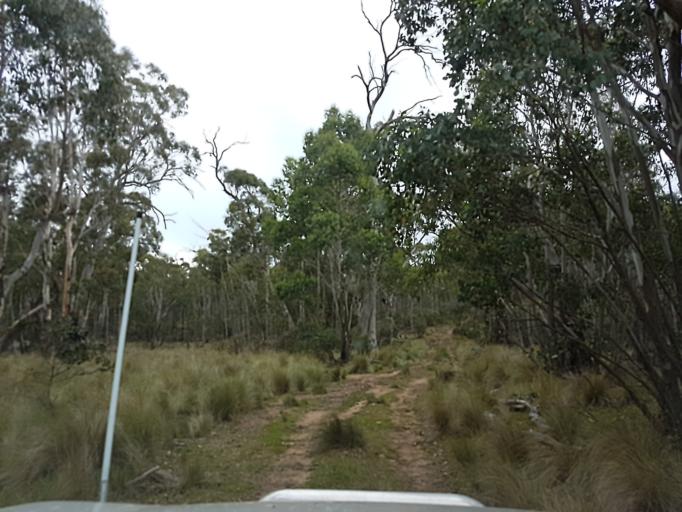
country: AU
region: New South Wales
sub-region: Snowy River
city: Jindabyne
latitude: -36.8532
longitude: 148.3347
